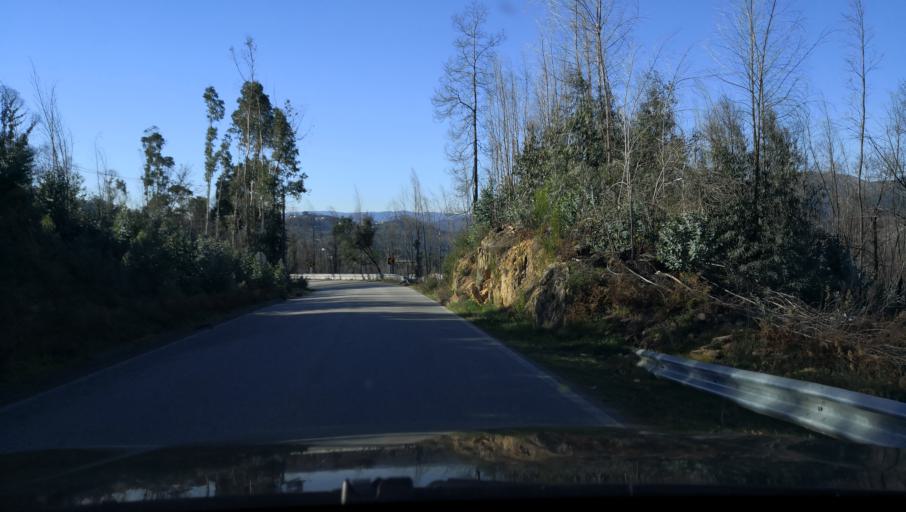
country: PT
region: Viseu
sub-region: Vouzela
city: Vouzela
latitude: 40.7308
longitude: -8.1432
